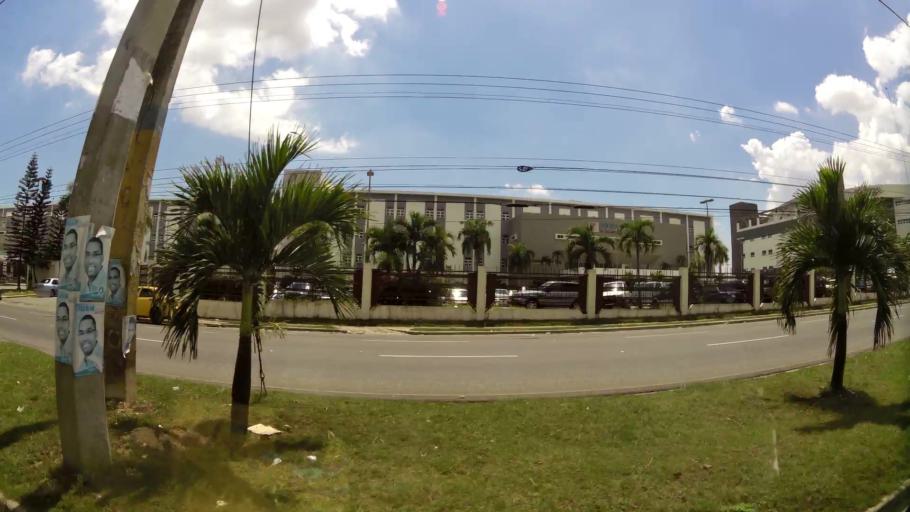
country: DO
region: Nacional
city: Ensanche Luperon
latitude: 18.5469
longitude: -69.8826
